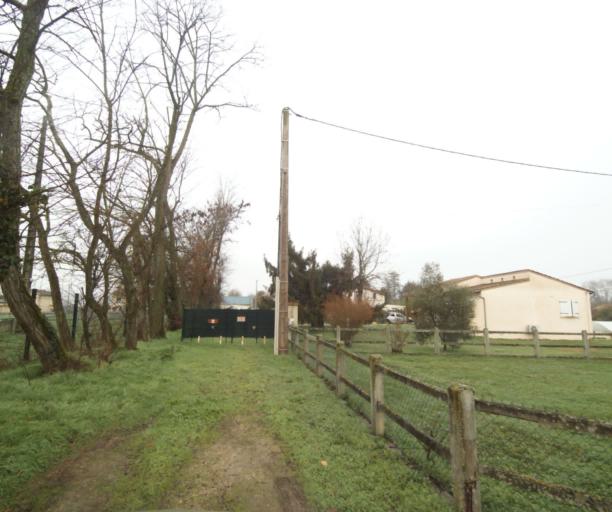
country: FR
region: Midi-Pyrenees
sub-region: Departement de la Haute-Garonne
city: Villemur-sur-Tarn
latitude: 43.8546
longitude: 1.5005
